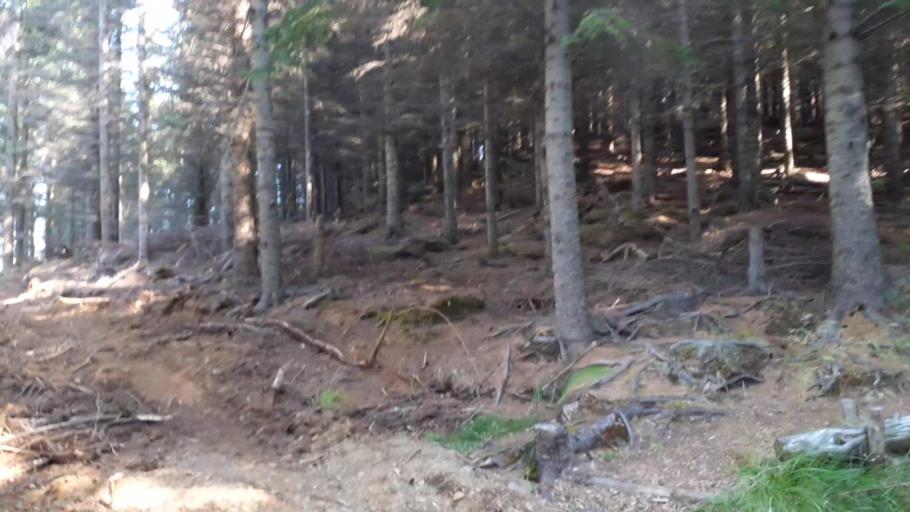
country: IS
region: West
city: Borgarnes
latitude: 64.6583
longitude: -21.7107
